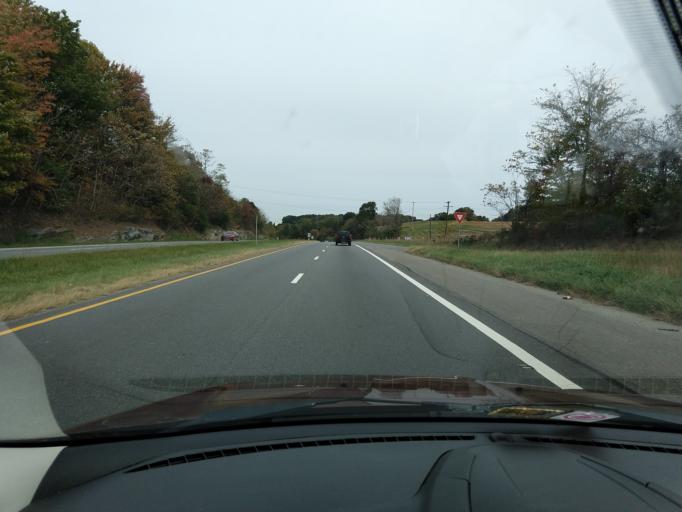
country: US
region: Virginia
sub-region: Franklin County
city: Rocky Mount
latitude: 37.0244
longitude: -79.8813
